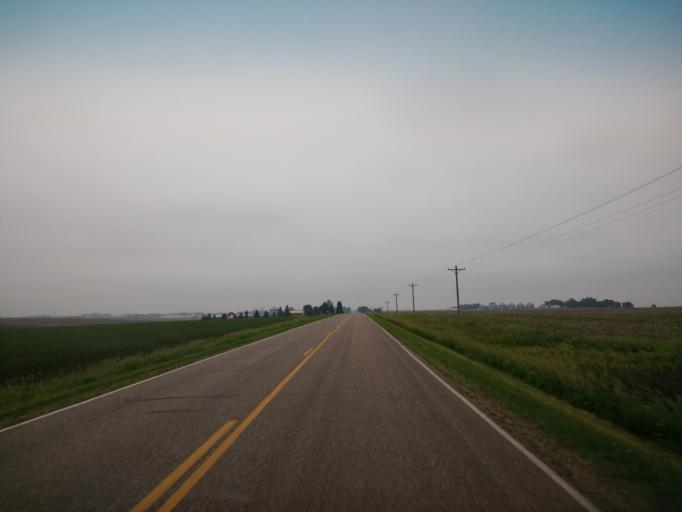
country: US
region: Iowa
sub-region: Sioux County
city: Alton
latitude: 43.0445
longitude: -95.8996
